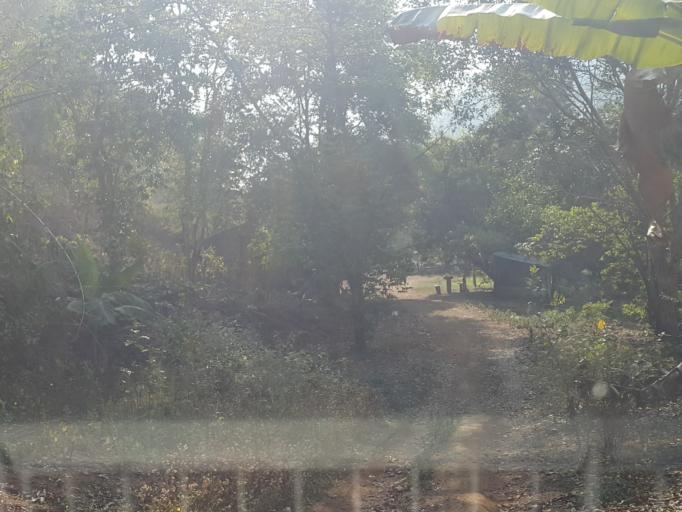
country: TH
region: Chiang Mai
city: Hang Dong
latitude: 18.7534
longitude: 98.8456
